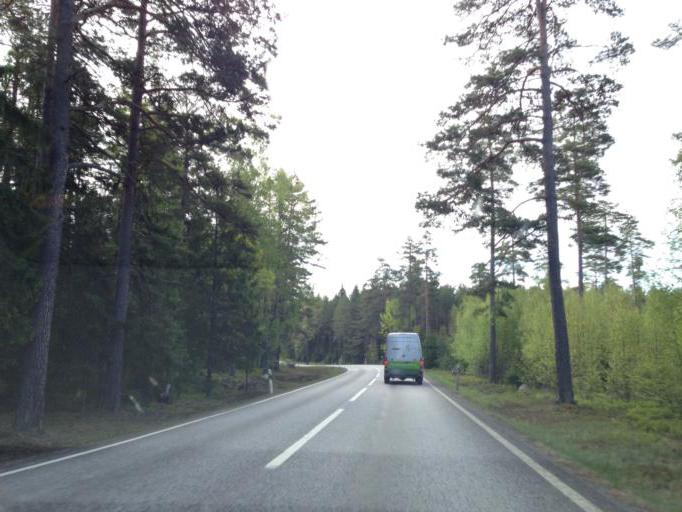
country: SE
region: Soedermanland
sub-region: Nykopings Kommun
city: Stigtomta
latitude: 58.8978
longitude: 16.8250
